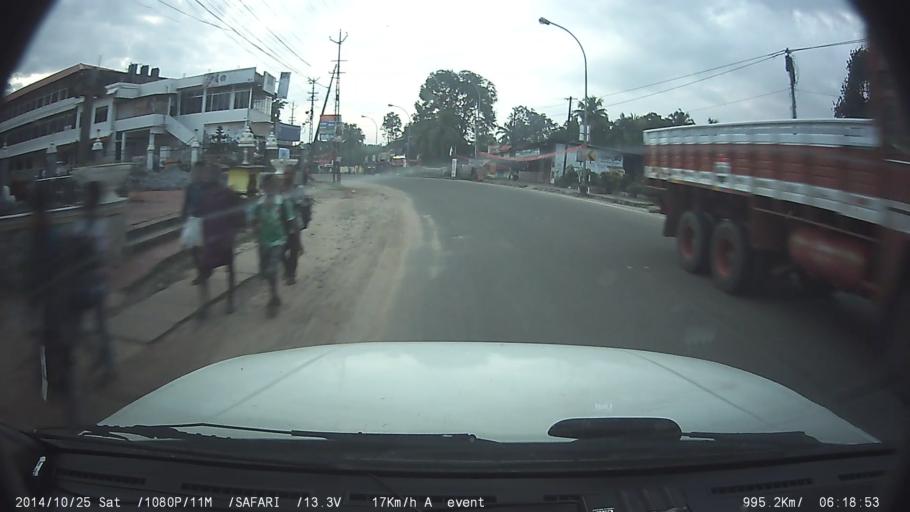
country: IN
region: Kerala
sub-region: Ernakulam
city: Perumpavur
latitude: 10.1114
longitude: 76.4793
